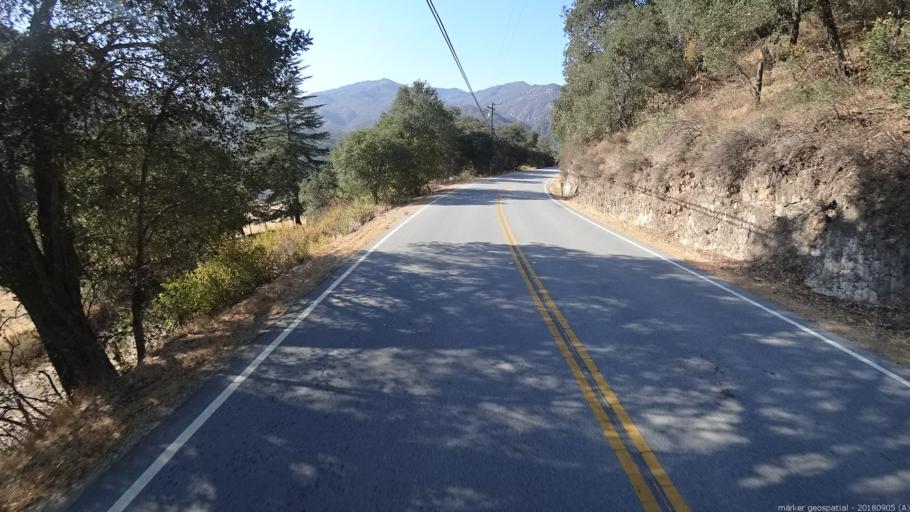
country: US
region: California
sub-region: Monterey County
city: Greenfield
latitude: 36.2432
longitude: -121.4323
